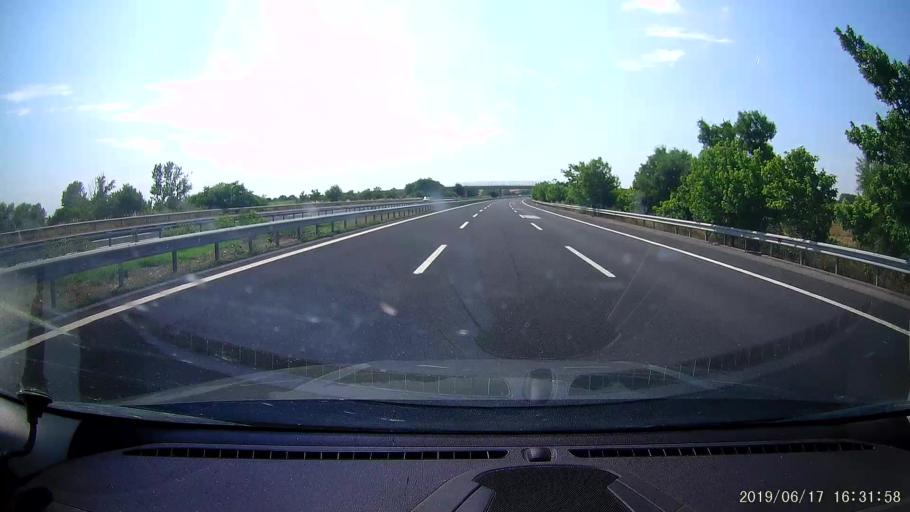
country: TR
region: Kirklareli
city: Buyukkaristiran
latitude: 41.3645
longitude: 27.6122
